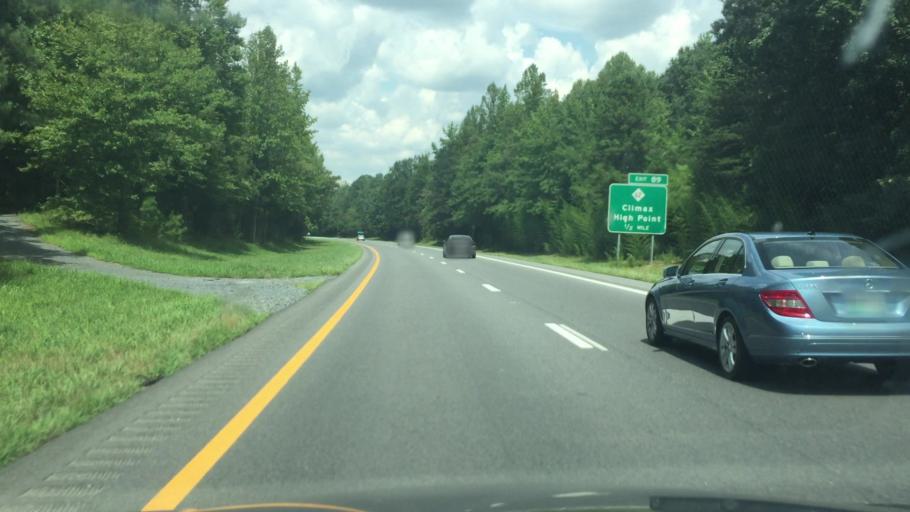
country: US
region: North Carolina
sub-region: Guilford County
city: Pleasant Garden
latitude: 35.9082
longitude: -79.8215
